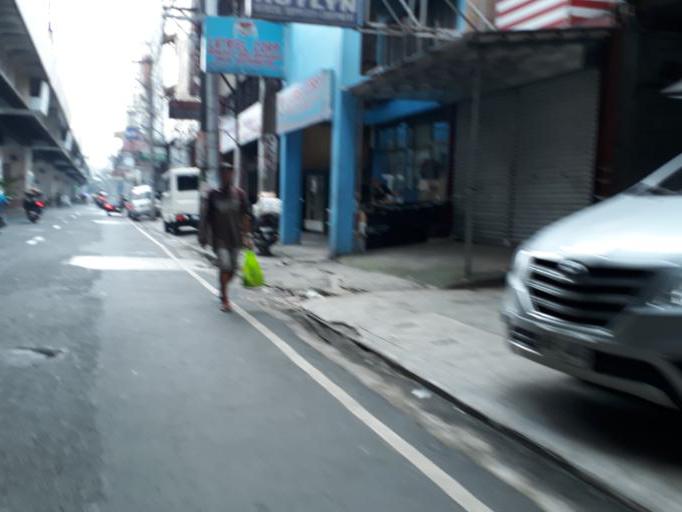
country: PH
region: Metro Manila
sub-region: City of Manila
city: Manila
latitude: 14.6112
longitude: 120.9826
